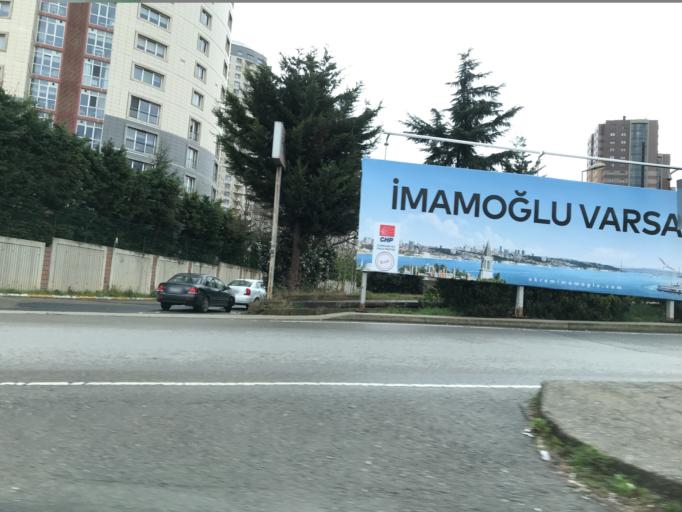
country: TR
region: Istanbul
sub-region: Atasehir
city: Atasehir
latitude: 40.9893
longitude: 29.1034
